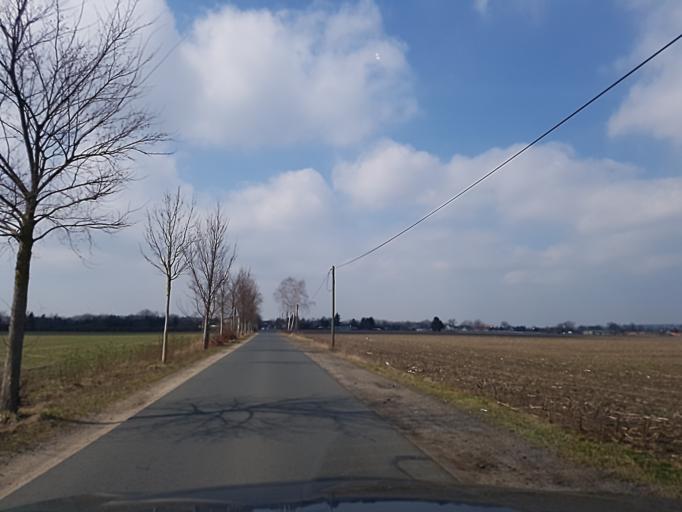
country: DE
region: Brandenburg
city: Elsterwerda
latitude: 51.4458
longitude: 13.5395
